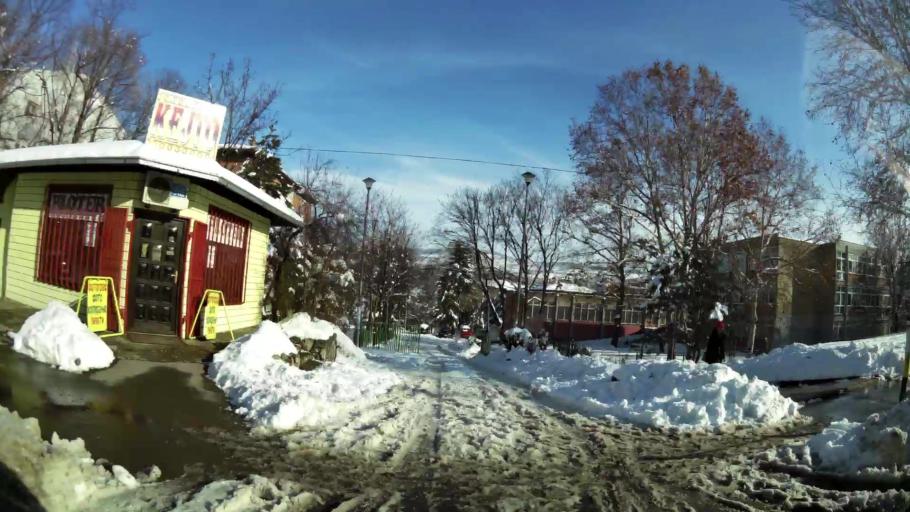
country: RS
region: Central Serbia
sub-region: Belgrade
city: Palilula
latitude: 44.8086
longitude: 20.5222
